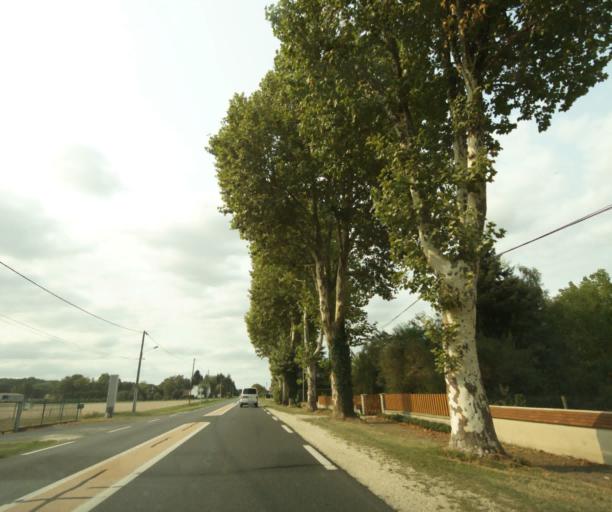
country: FR
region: Centre
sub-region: Departement de l'Indre
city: Chatillon-sur-Indre
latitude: 47.0229
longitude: 1.1050
